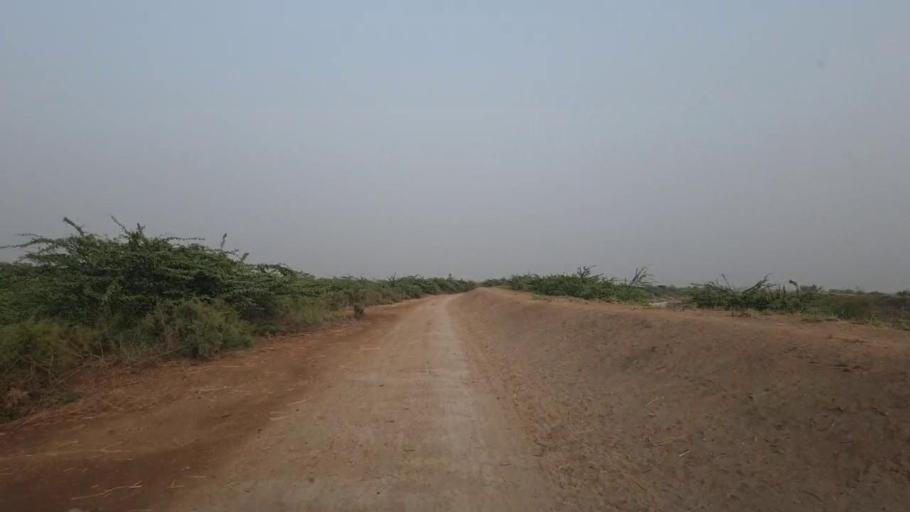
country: PK
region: Sindh
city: Mirpur Batoro
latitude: 24.6421
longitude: 68.3792
